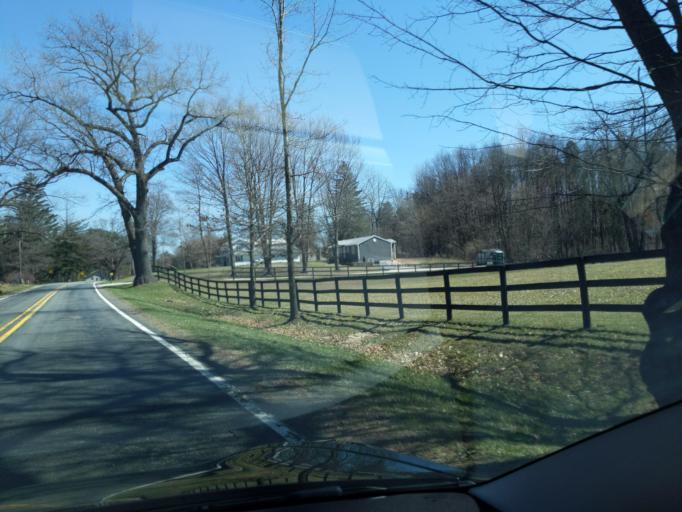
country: US
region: Michigan
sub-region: Ingham County
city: Mason
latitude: 42.5342
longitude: -84.3389
